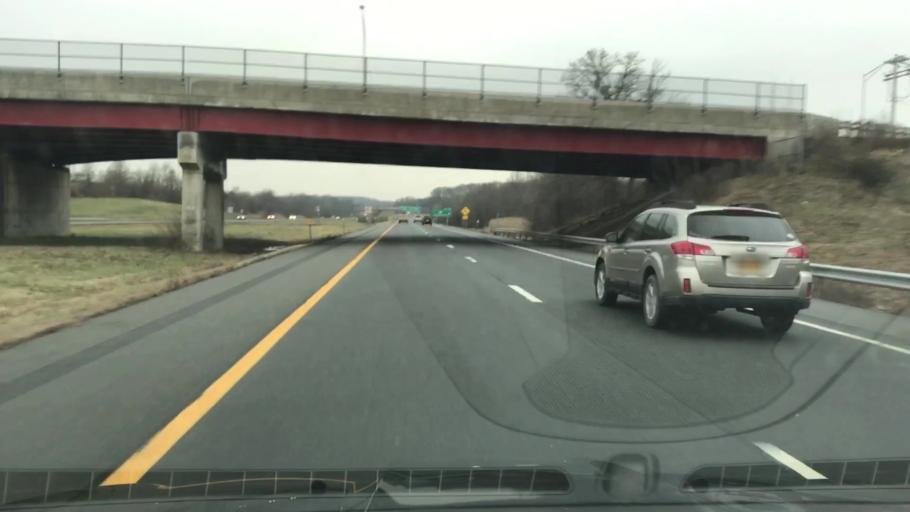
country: US
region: New York
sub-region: Orange County
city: Scotchtown
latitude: 41.4537
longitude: -74.3581
